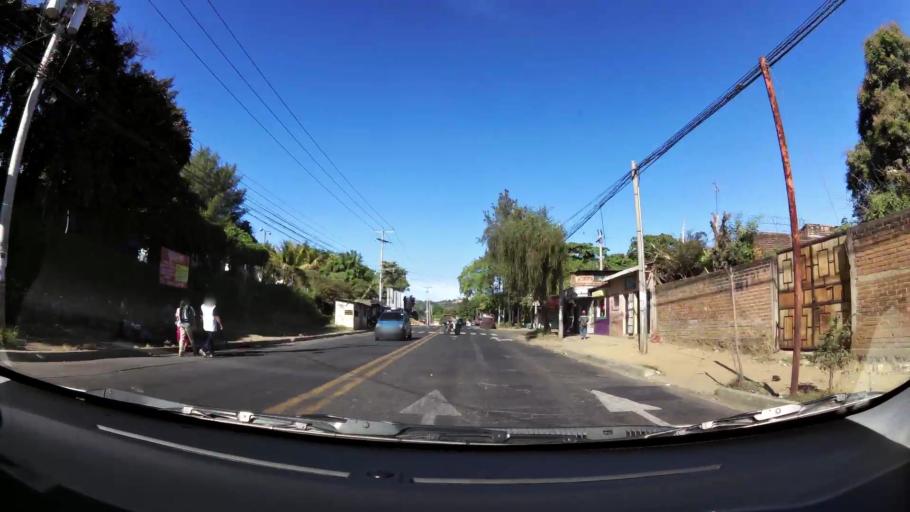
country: SV
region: Santa Ana
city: Santa Ana
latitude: 13.9803
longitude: -89.5630
